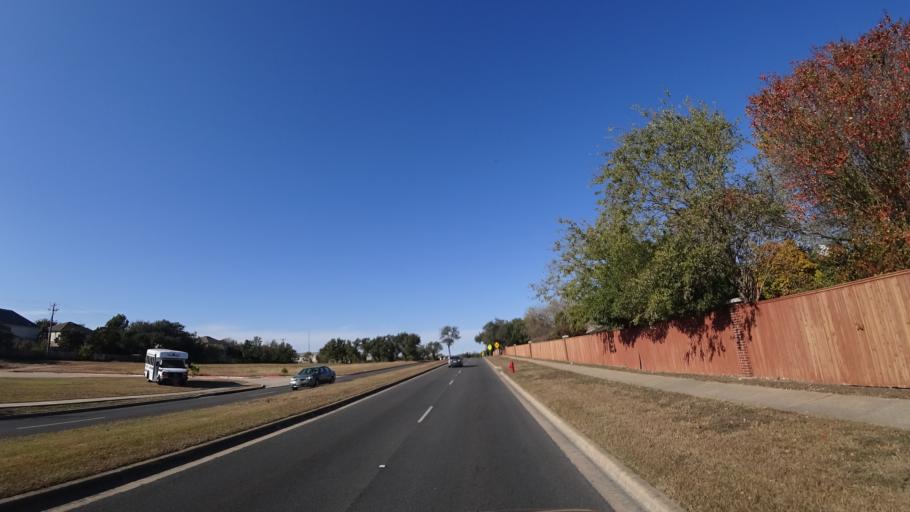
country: US
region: Texas
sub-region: Williamson County
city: Cedar Park
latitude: 30.5189
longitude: -97.8529
